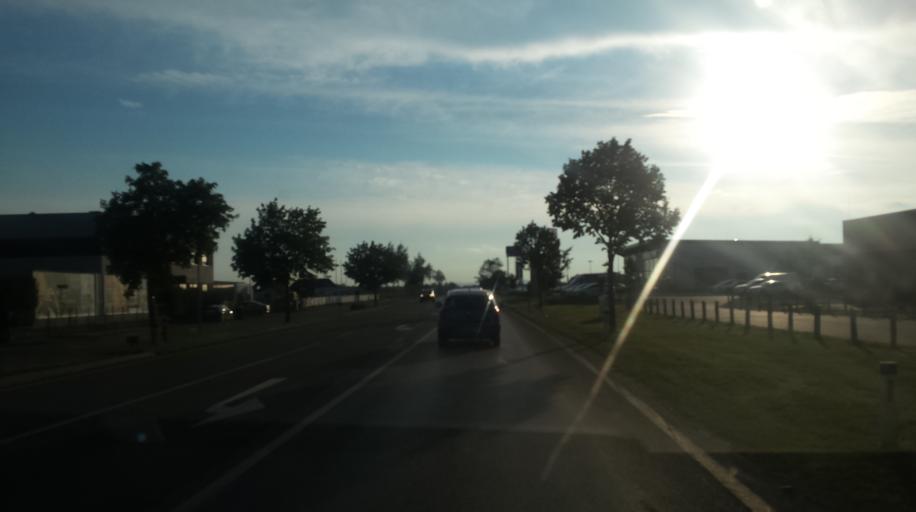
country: AT
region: Lower Austria
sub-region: Politischer Bezirk Ganserndorf
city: Parbasdorf
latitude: 48.3119
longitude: 16.6095
